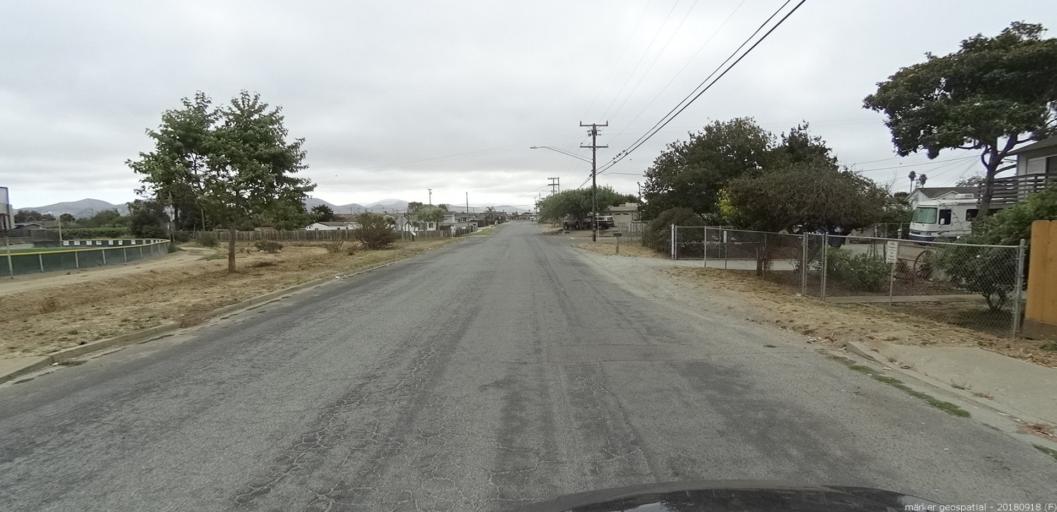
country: US
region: California
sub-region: Monterey County
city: Boronda
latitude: 36.7343
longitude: -121.6418
